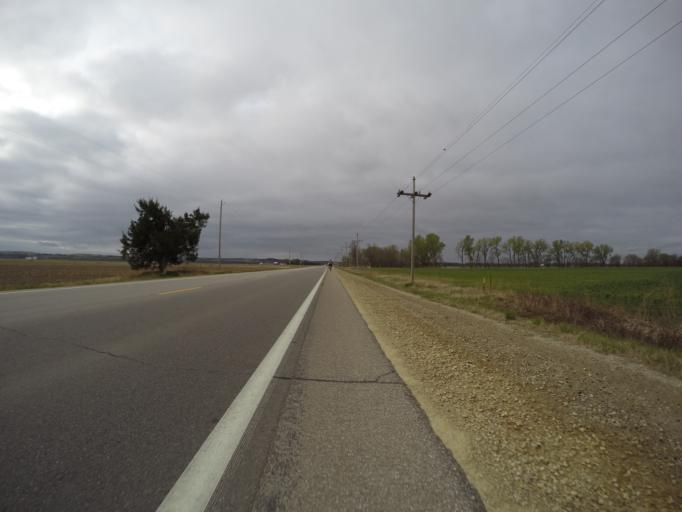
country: US
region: Kansas
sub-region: Pottawatomie County
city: Wamego
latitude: 39.1759
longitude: -96.3055
